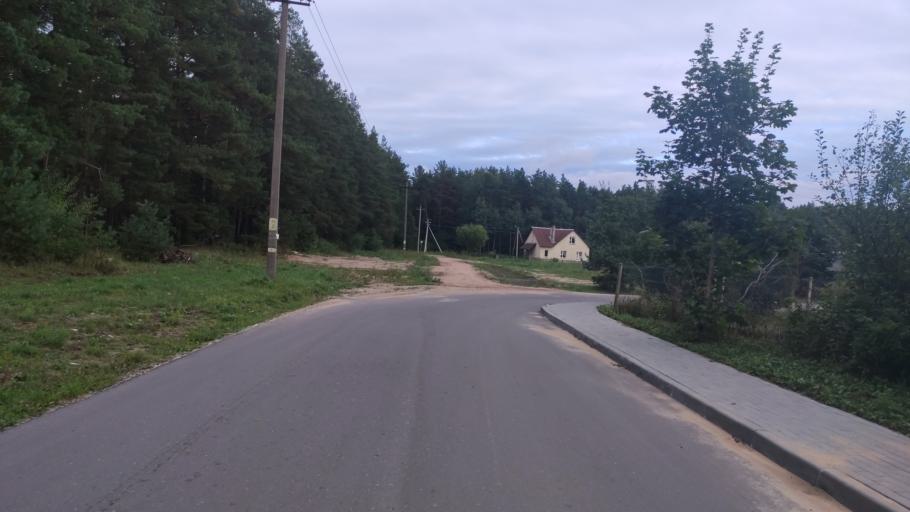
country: BY
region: Minsk
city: Narach
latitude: 54.9313
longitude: 26.6987
